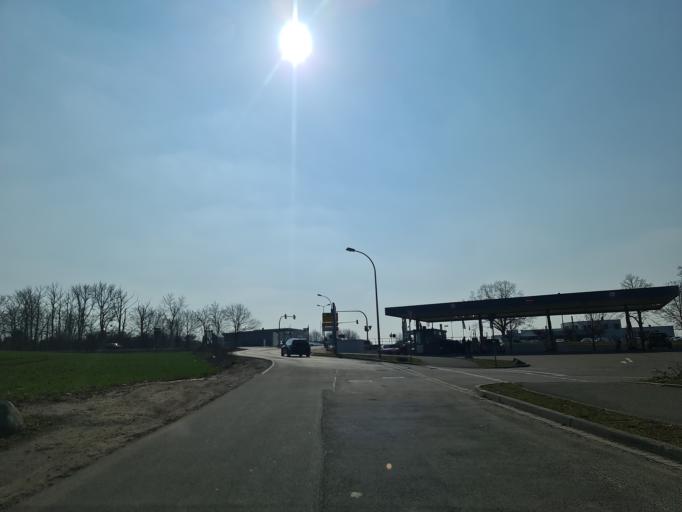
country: DE
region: Saxony-Anhalt
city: Zeitz
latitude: 51.0363
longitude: 12.1292
